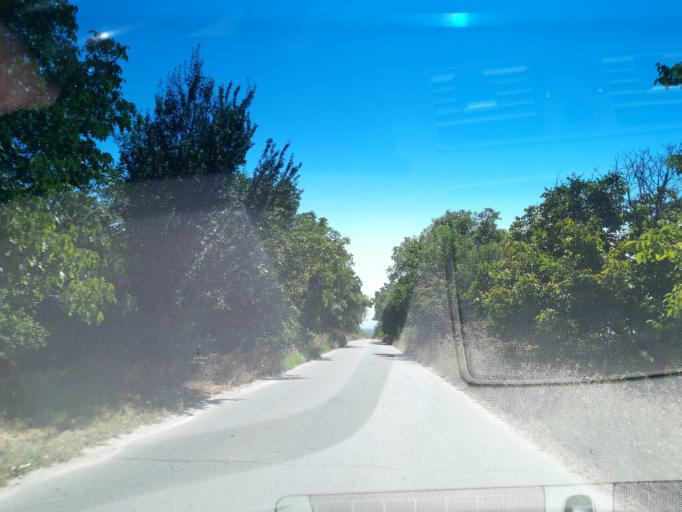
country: BG
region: Pazardzhik
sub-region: Obshtina Pazardzhik
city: Pazardzhik
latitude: 42.2991
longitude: 24.3979
